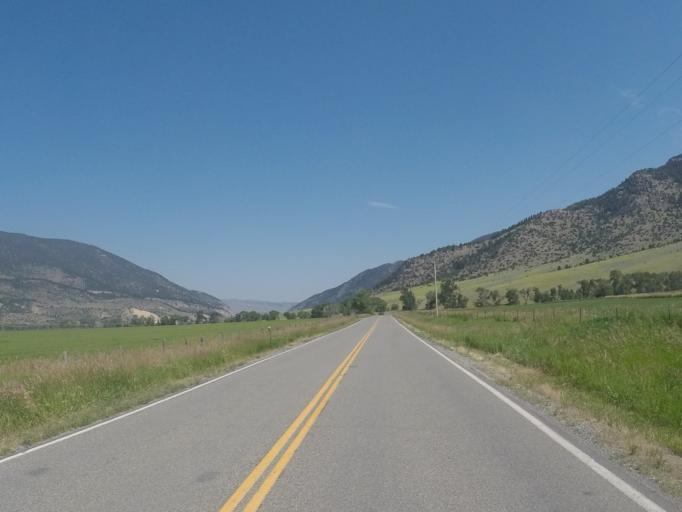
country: US
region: Montana
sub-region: Park County
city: Livingston
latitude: 45.5632
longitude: -110.5588
